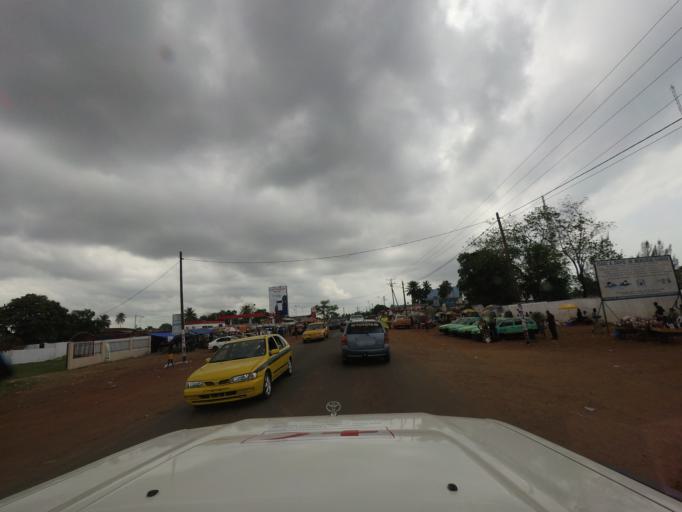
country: LR
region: Montserrado
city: Monrovia
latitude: 6.2647
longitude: -10.7014
